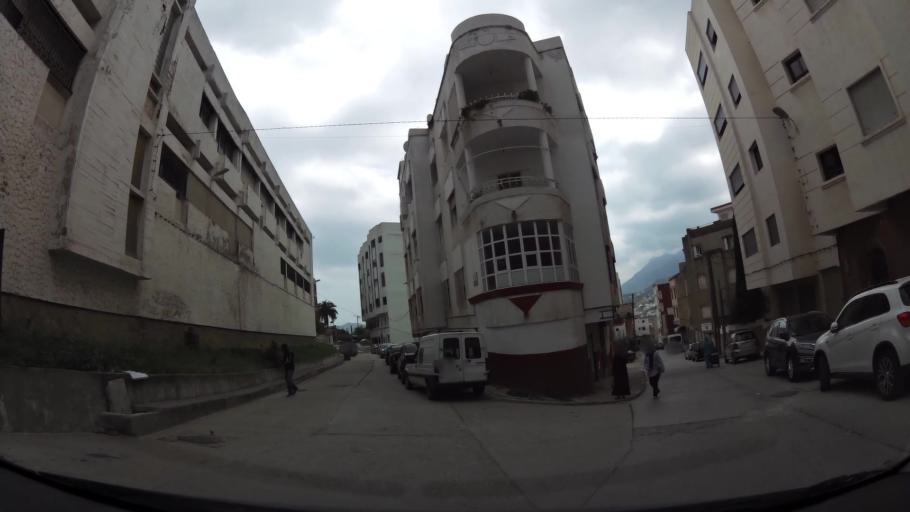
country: MA
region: Tanger-Tetouan
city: Tetouan
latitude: 35.5679
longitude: -5.3800
